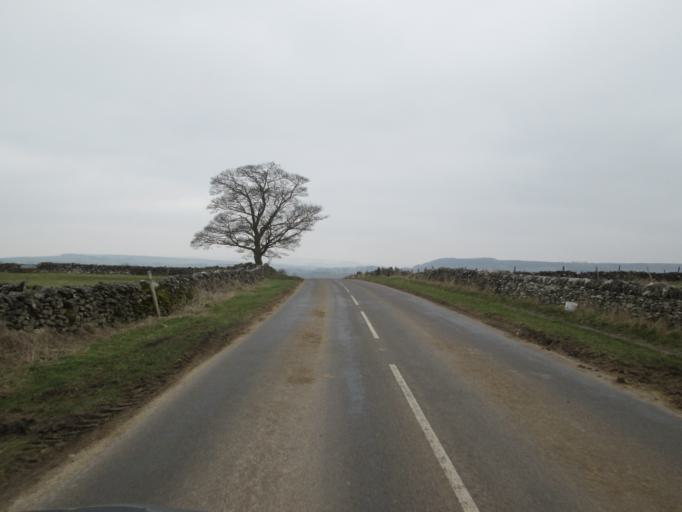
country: GB
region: England
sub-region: Derbyshire
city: Tideswell
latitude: 53.2631
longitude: -1.7250
